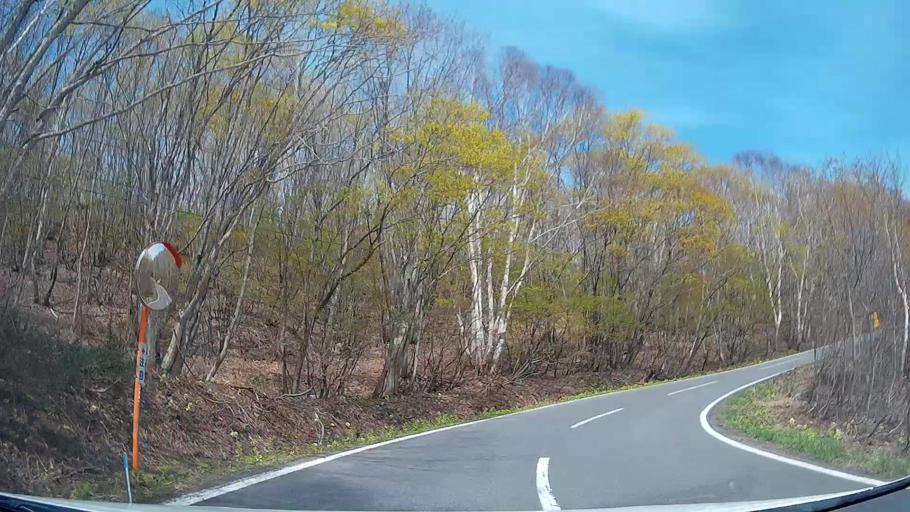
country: JP
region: Iwate
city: Shizukuishi
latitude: 39.9330
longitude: 140.9560
